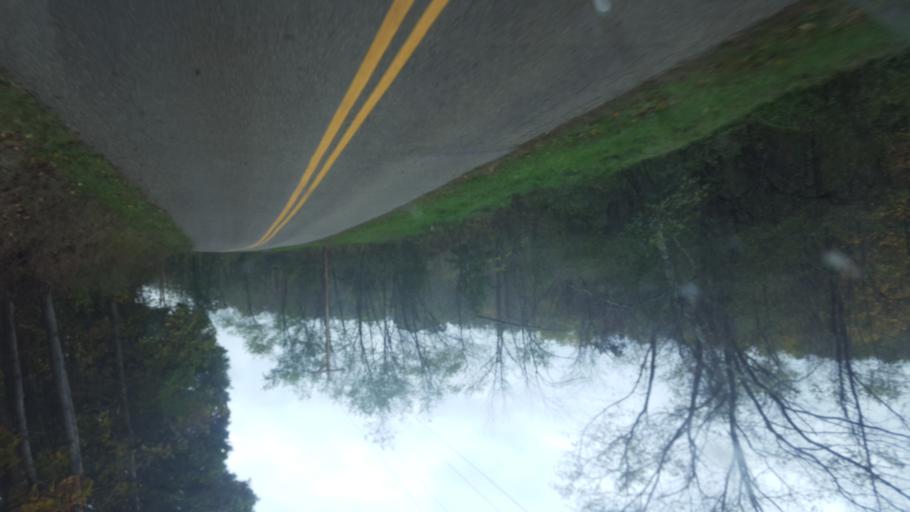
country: US
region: Ohio
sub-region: Carroll County
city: Carrollton
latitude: 40.4811
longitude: -81.0794
